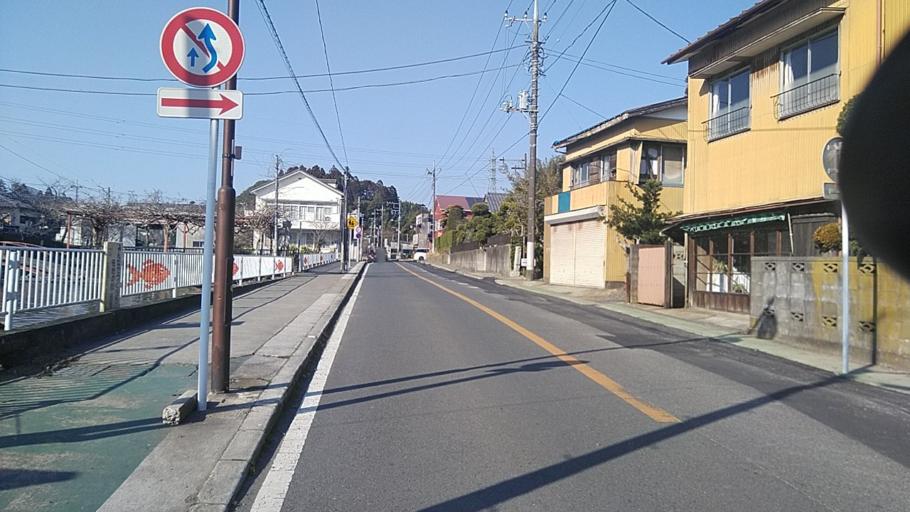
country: JP
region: Chiba
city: Yokaichiba
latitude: 35.7039
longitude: 140.5462
